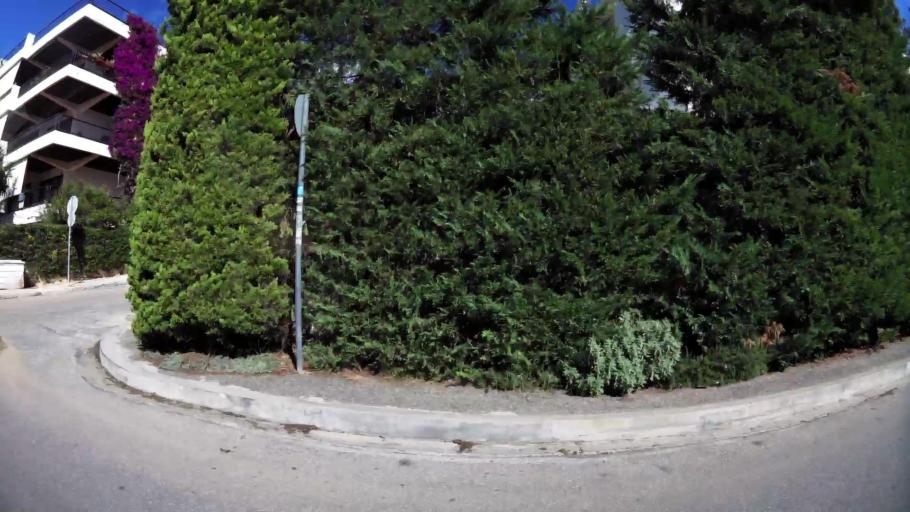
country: GR
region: Attica
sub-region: Nomarchia Anatolikis Attikis
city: Voula
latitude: 37.8393
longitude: 23.7775
